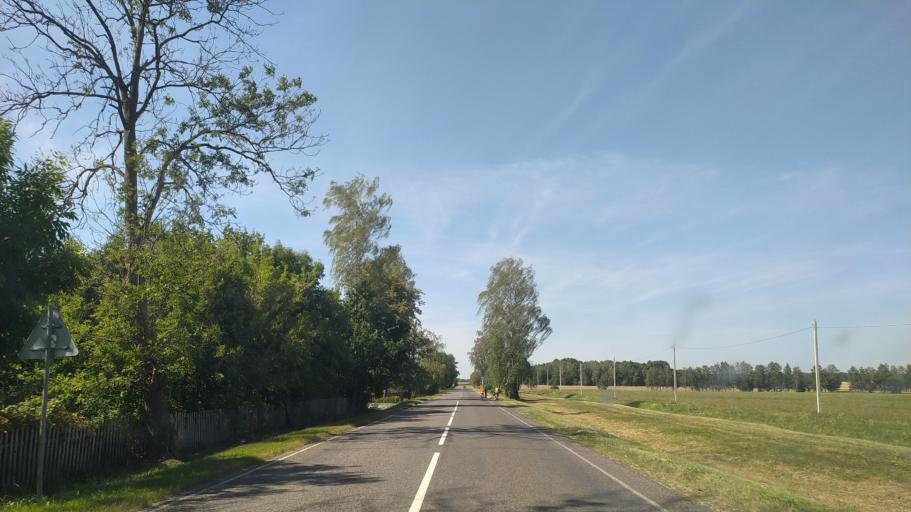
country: BY
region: Brest
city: Byaroza
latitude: 52.3915
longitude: 25.0149
